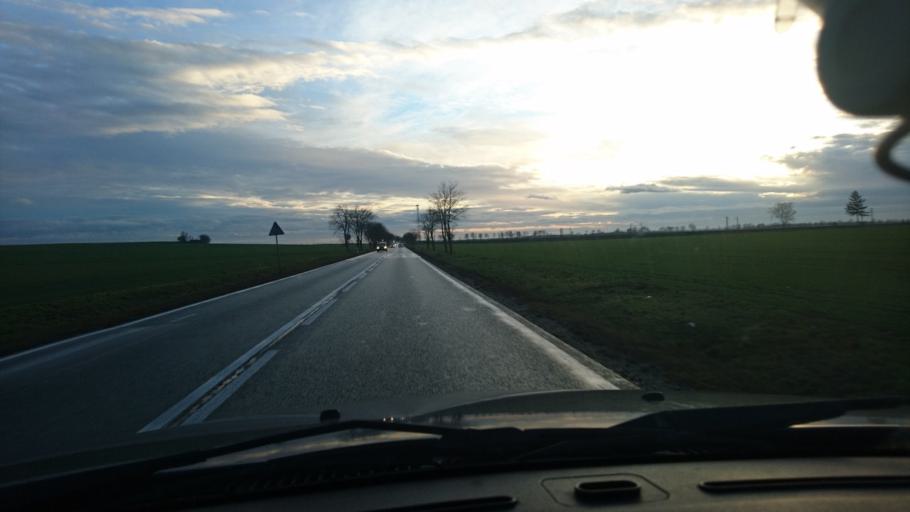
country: PL
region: Opole Voivodeship
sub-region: Powiat kluczborski
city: Byczyna
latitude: 51.1044
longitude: 18.2063
